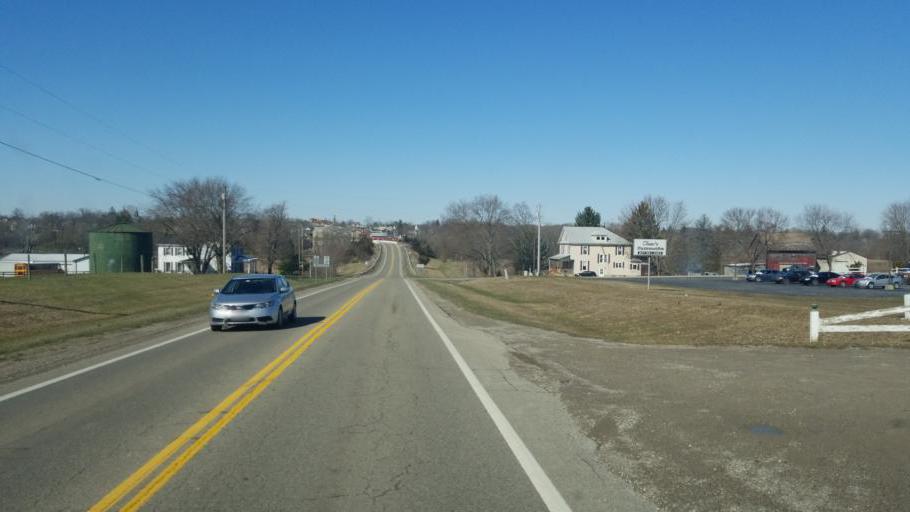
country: US
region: Ohio
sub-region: Highland County
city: Greenfield
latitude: 39.3530
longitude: -83.3710
